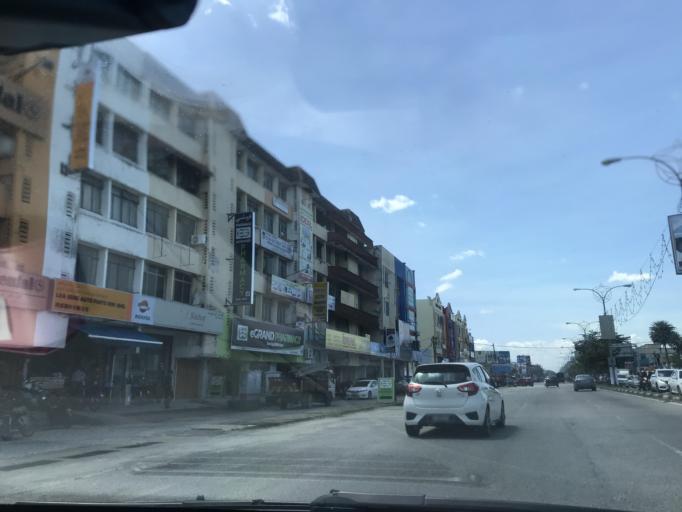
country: MY
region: Kelantan
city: Kota Bharu
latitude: 6.1091
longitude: 102.2554
